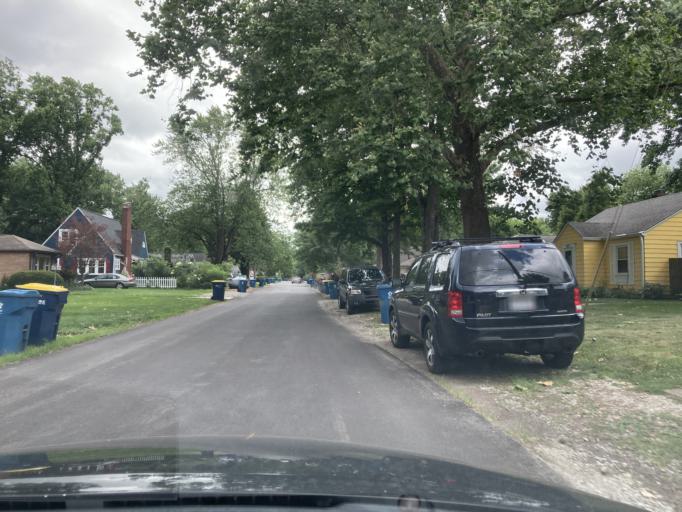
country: US
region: Indiana
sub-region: Marion County
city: Broad Ripple
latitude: 39.8618
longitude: -86.1330
